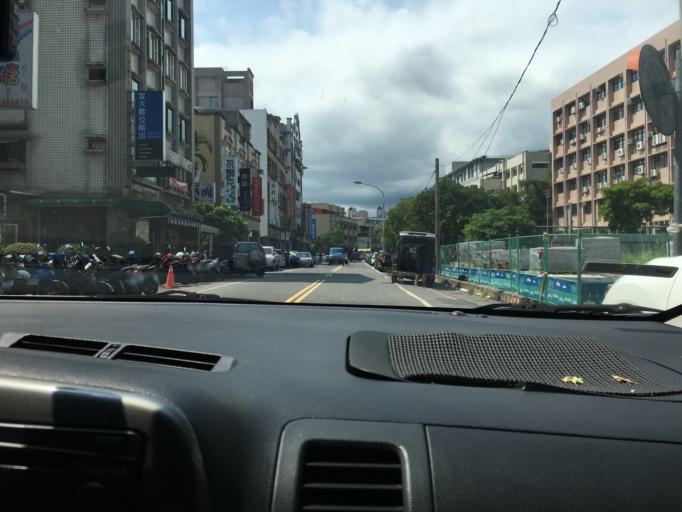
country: TW
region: Taiwan
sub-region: Yilan
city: Yilan
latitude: 24.7449
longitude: 121.7459
